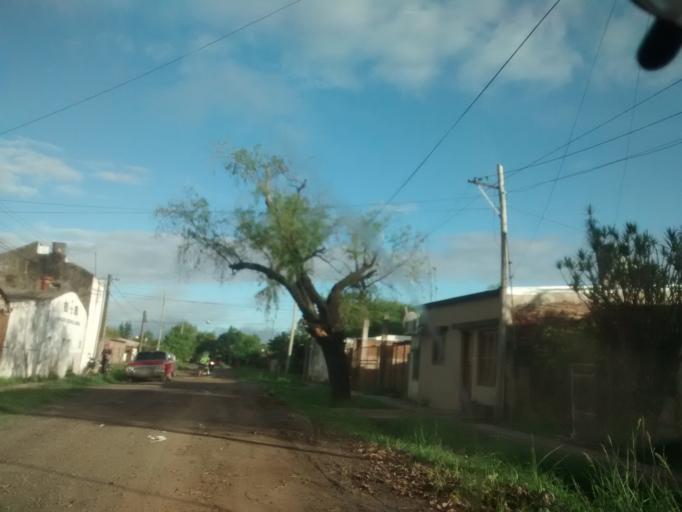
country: AR
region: Chaco
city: Resistencia
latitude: -27.4529
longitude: -59.0053
